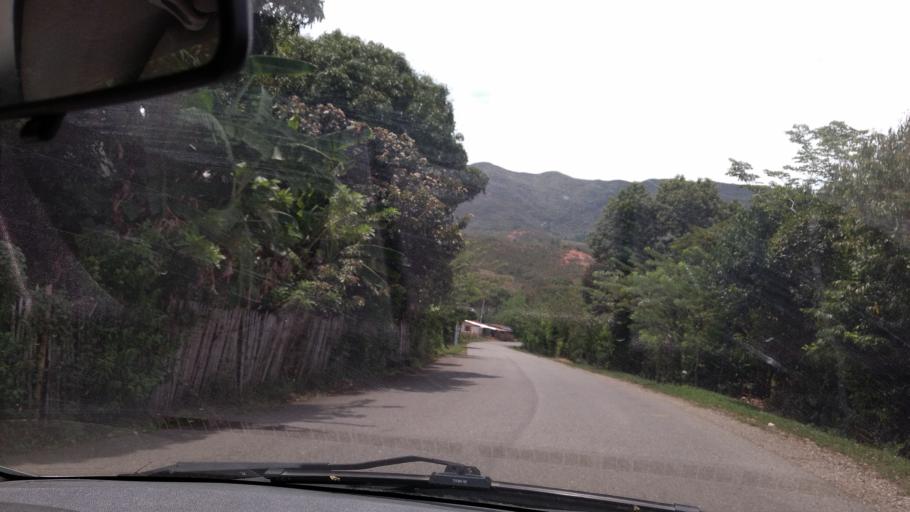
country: CO
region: Cauca
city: Buenos Aires
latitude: 3.0563
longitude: -76.6569
